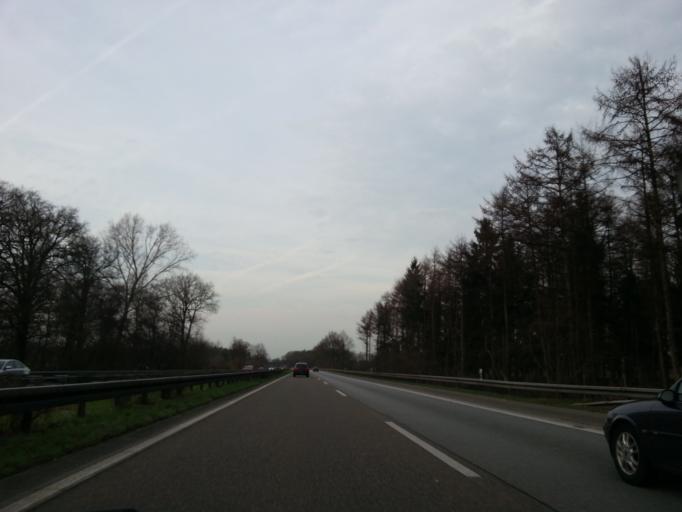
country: DE
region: North Rhine-Westphalia
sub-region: Regierungsbezirk Munster
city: Isselburg
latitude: 51.7922
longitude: 6.4961
